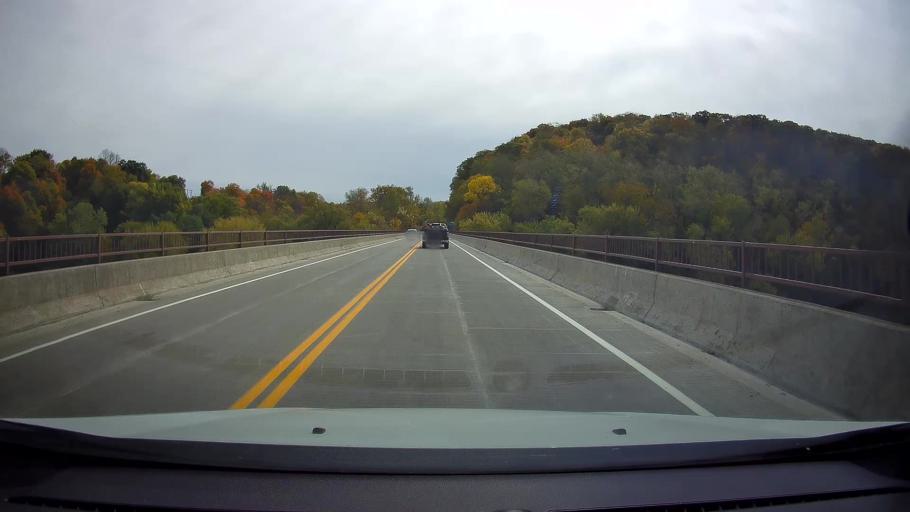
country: US
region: Wisconsin
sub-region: Polk County
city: Osceola
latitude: 45.3217
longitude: -92.7105
